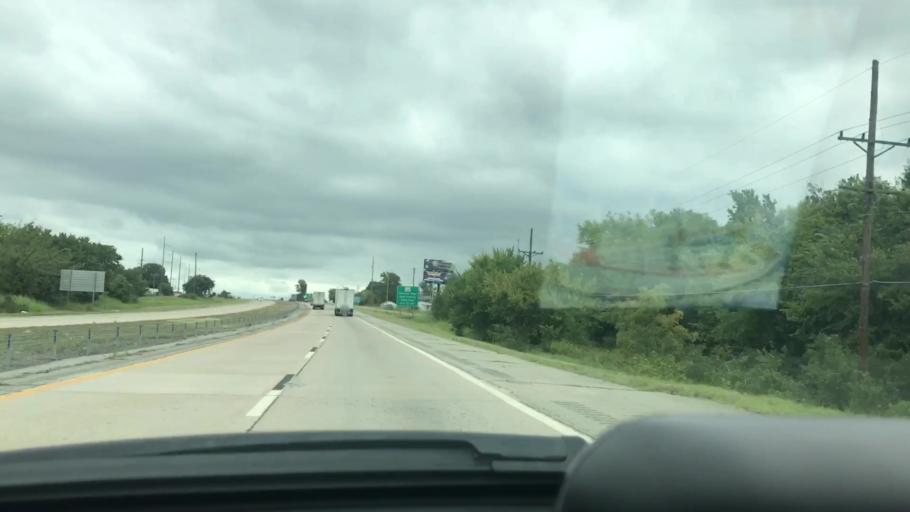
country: US
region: Oklahoma
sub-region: McIntosh County
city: Eufaula
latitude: 35.3522
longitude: -95.5774
